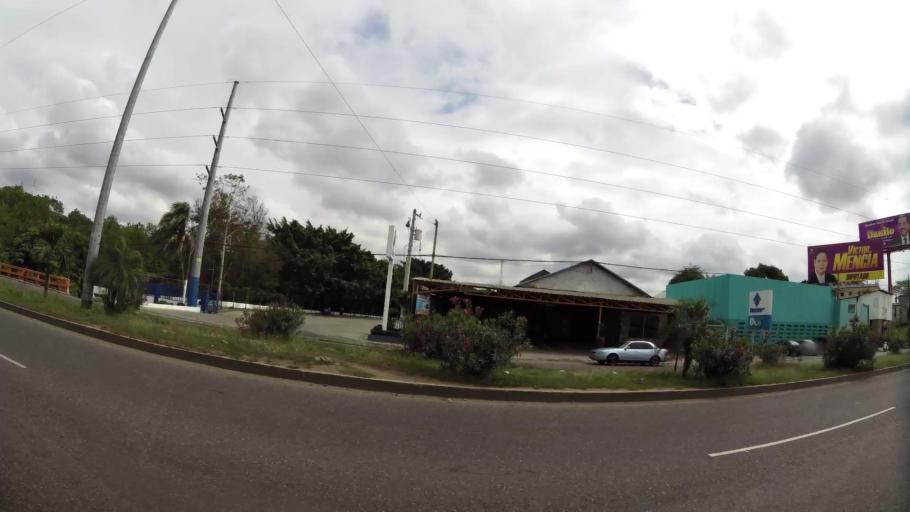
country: DO
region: Santiago
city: Santiago de los Caballeros
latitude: 19.4417
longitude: -70.6686
